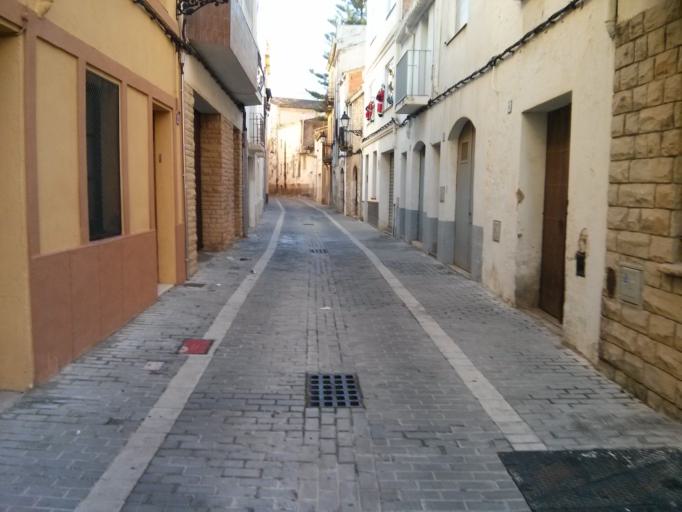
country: ES
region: Catalonia
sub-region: Provincia de Tarragona
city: El Vendrell
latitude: 41.2222
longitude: 1.5329
